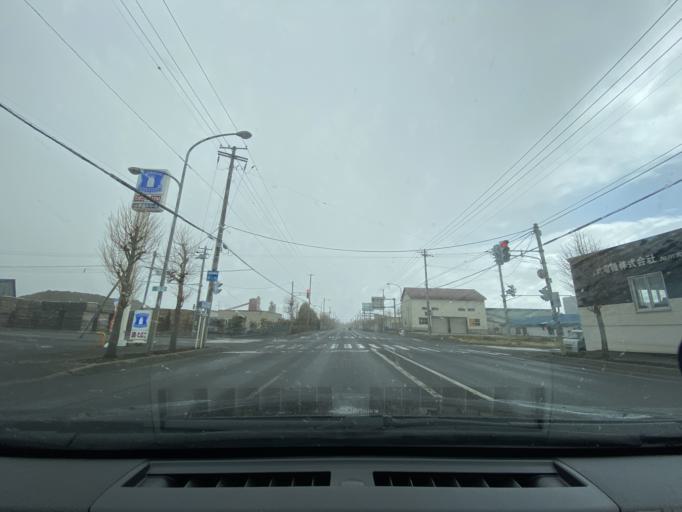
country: JP
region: Hokkaido
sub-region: Asahikawa-shi
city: Asahikawa
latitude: 43.8241
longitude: 142.4192
